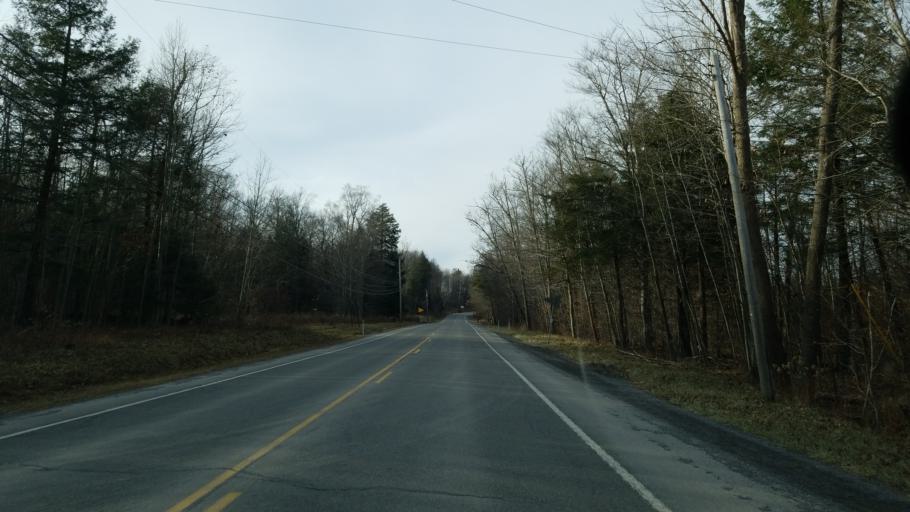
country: US
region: Pennsylvania
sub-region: Clearfield County
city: DuBois
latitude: 41.0307
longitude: -78.6803
